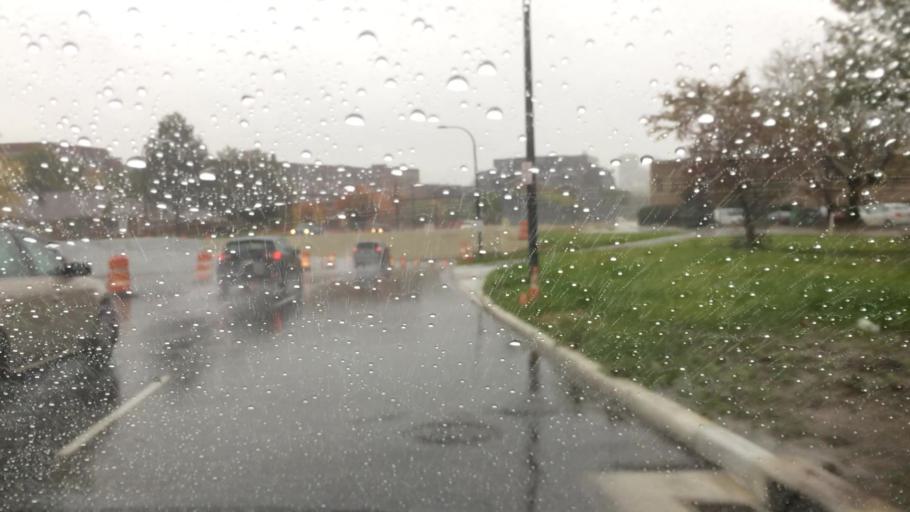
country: US
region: Ohio
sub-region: Summit County
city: Akron
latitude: 41.0676
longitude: -81.5262
